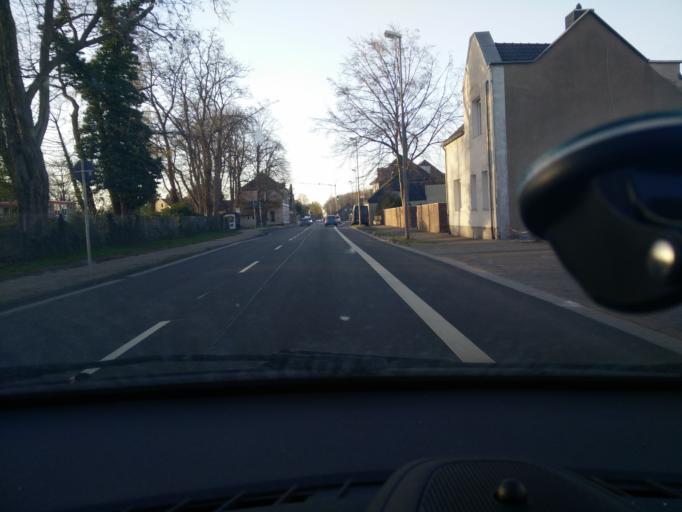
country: DE
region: North Rhine-Westphalia
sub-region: Regierungsbezirk Dusseldorf
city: Moers
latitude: 51.4242
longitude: 6.6528
